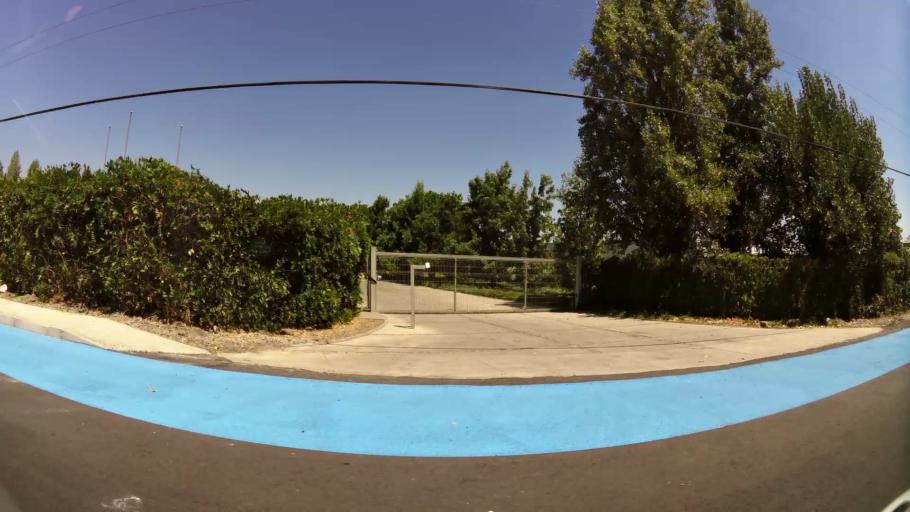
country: CL
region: Maule
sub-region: Provincia de Curico
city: Curico
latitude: -34.9879
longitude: -71.2121
